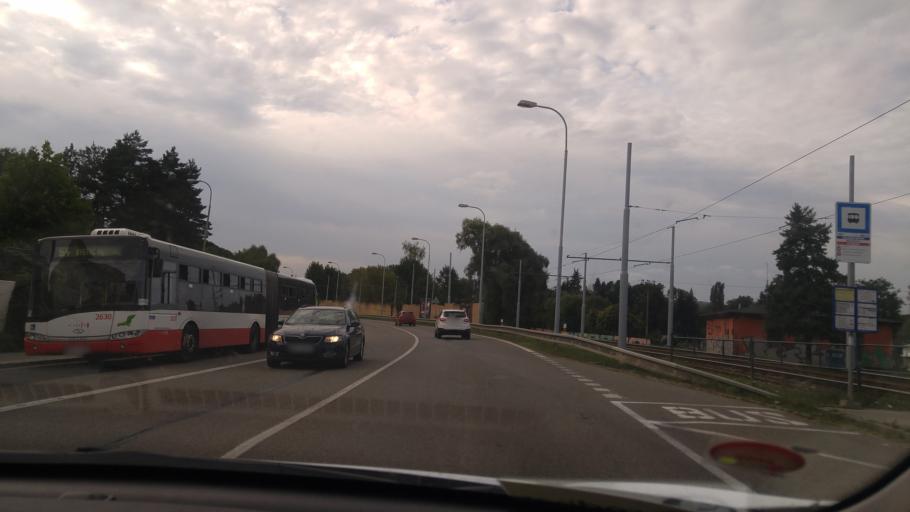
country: CZ
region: South Moravian
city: Troubsko
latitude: 49.2284
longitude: 16.5312
